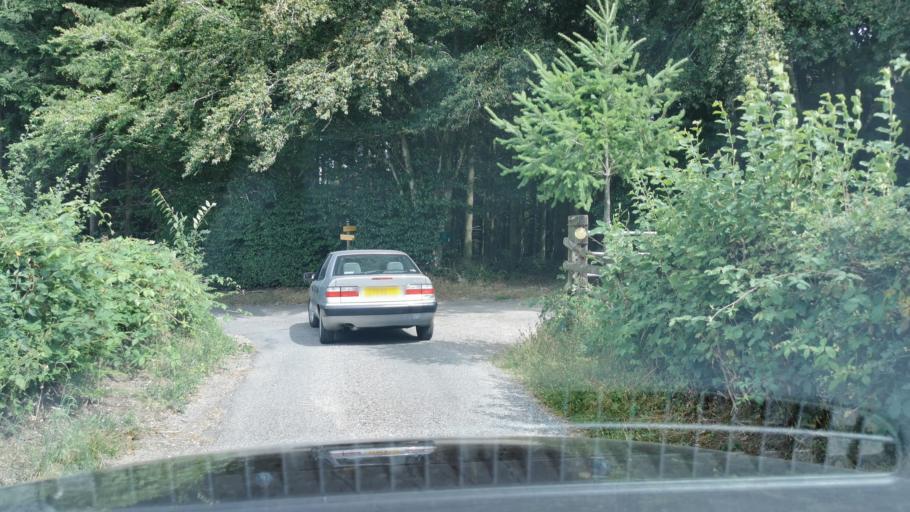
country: FR
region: Bourgogne
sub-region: Departement de Saone-et-Loire
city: Marmagne
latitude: 46.8083
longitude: 4.2839
